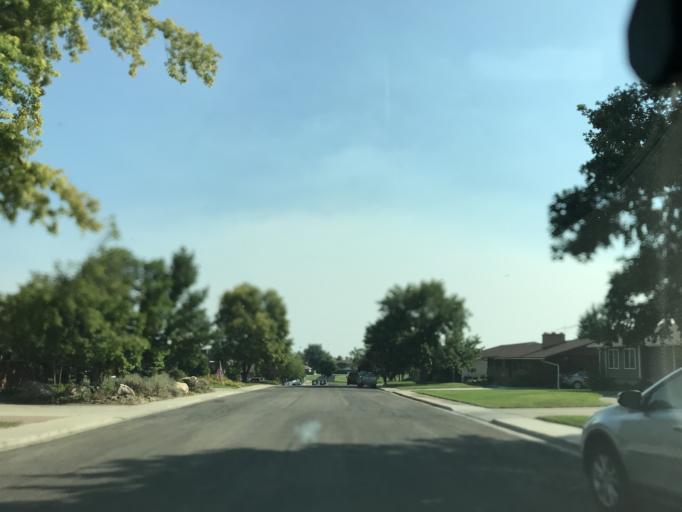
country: US
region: Utah
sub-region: Utah County
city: Orem
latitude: 40.2818
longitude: -111.7013
